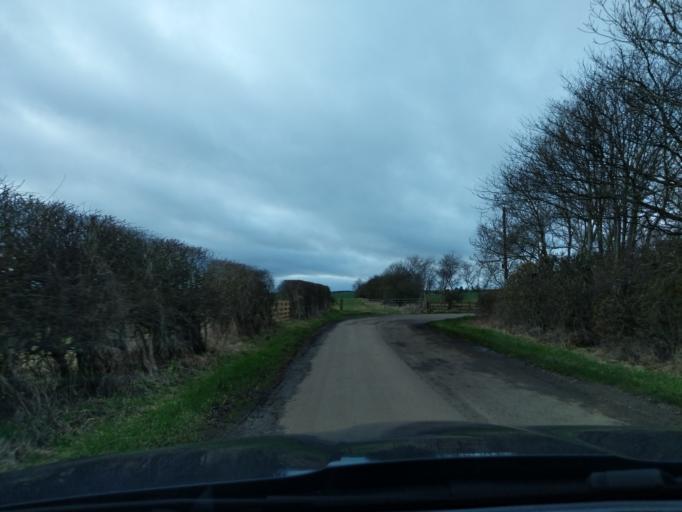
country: GB
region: England
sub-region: Northumberland
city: Ancroft
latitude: 55.7026
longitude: -2.0242
